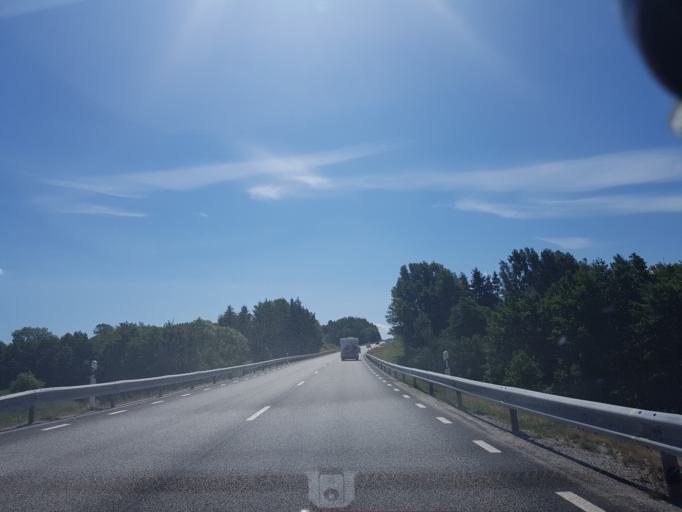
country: SE
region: Vaestra Goetaland
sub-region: Orust
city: Henan
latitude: 58.1410
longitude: 11.6440
